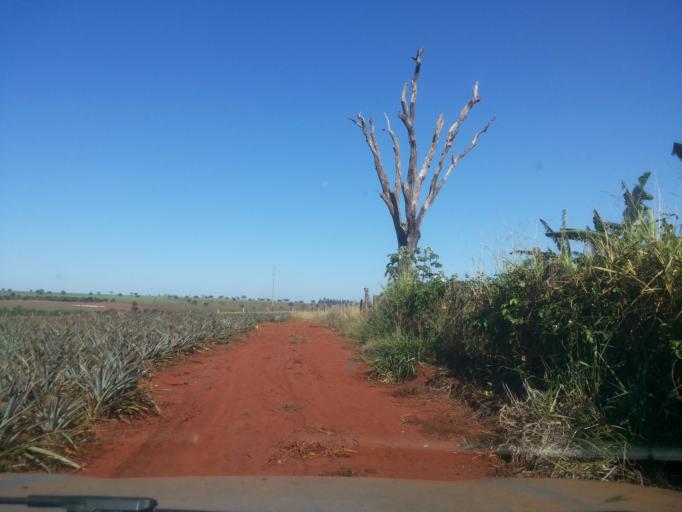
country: BR
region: Minas Gerais
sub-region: Centralina
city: Centralina
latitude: -18.7632
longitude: -49.2036
